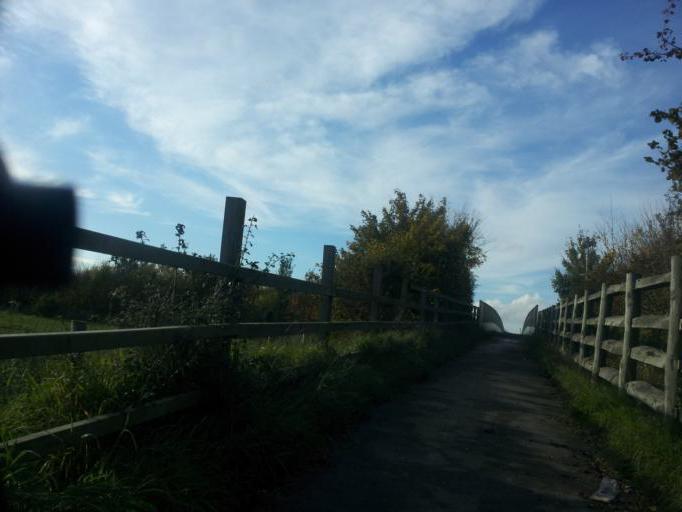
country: GB
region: England
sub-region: Kent
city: Sittingbourne
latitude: 51.3624
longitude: 0.7288
